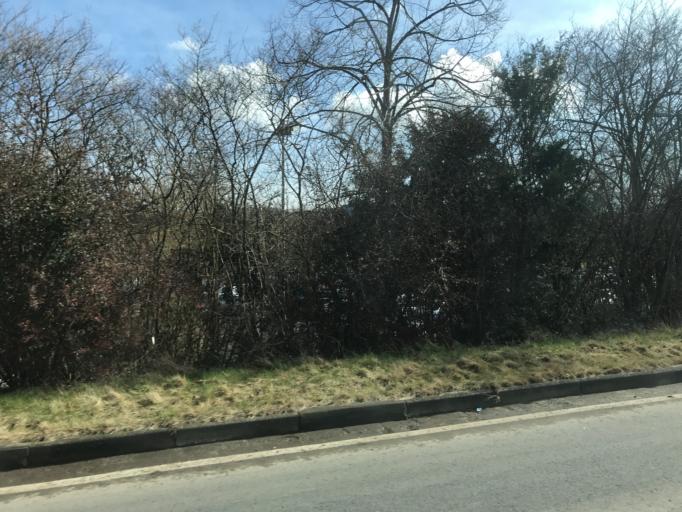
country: DE
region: Rheinland-Pfalz
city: Bell
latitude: 50.4038
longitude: 7.2533
